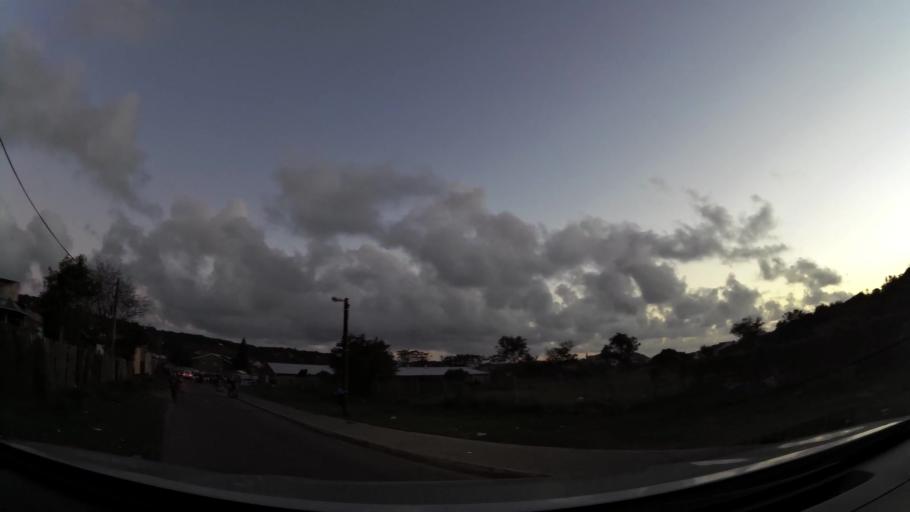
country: ZA
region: Western Cape
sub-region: Eden District Municipality
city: Knysna
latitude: -34.0256
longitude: 22.8125
